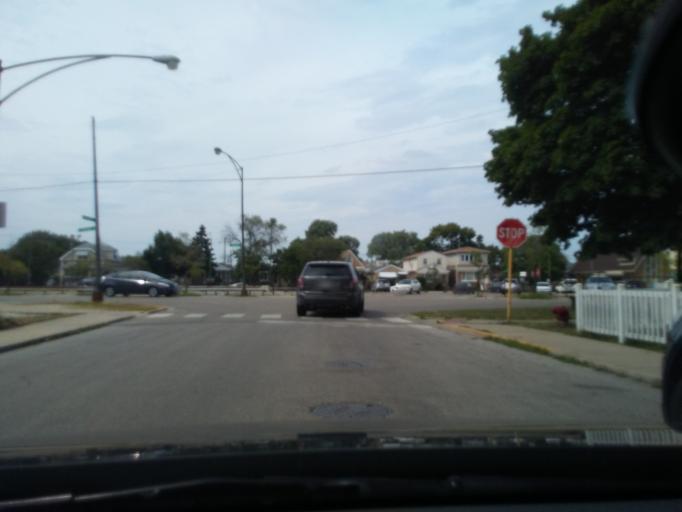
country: US
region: Illinois
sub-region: Cook County
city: Harwood Heights
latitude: 41.9748
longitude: -87.7843
